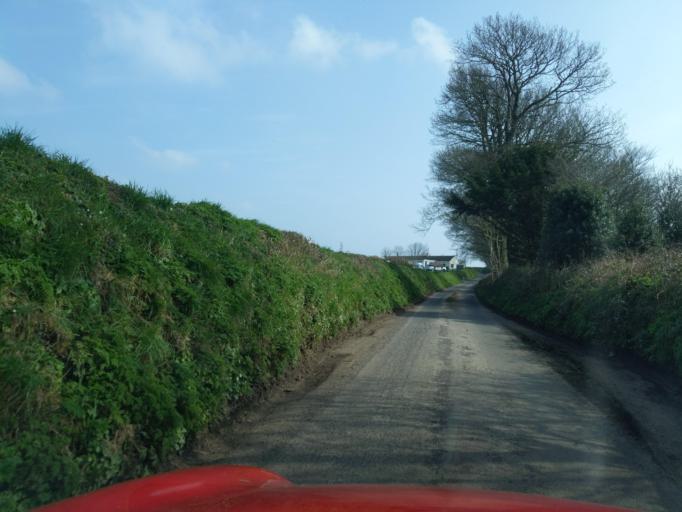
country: GB
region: England
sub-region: Devon
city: Kingsbridge
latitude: 50.3104
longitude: -3.7713
